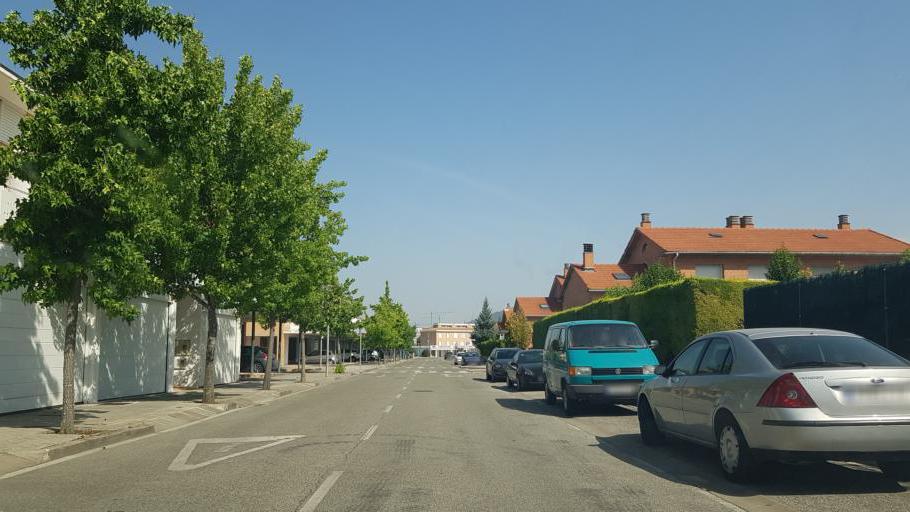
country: ES
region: Navarre
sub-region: Provincia de Navarra
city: Segundo Ensanche
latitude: 42.7929
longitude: -1.6238
